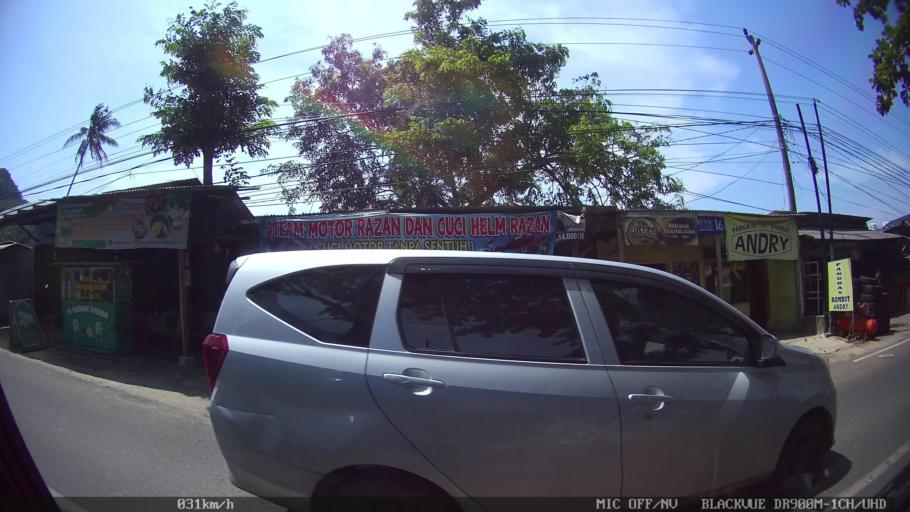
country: ID
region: Lampung
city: Kedaton
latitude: -5.3901
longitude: 105.2740
